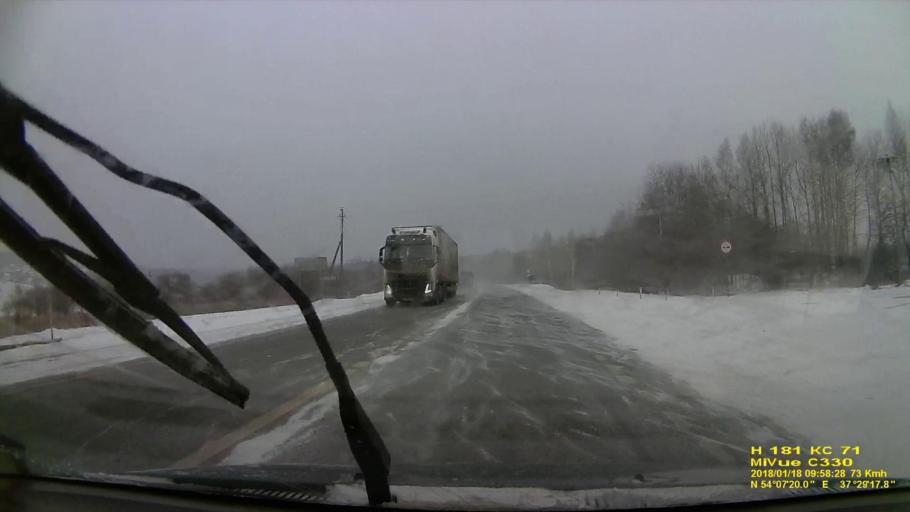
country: RU
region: Tula
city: Kosaya Gora
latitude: 54.1220
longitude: 37.4882
